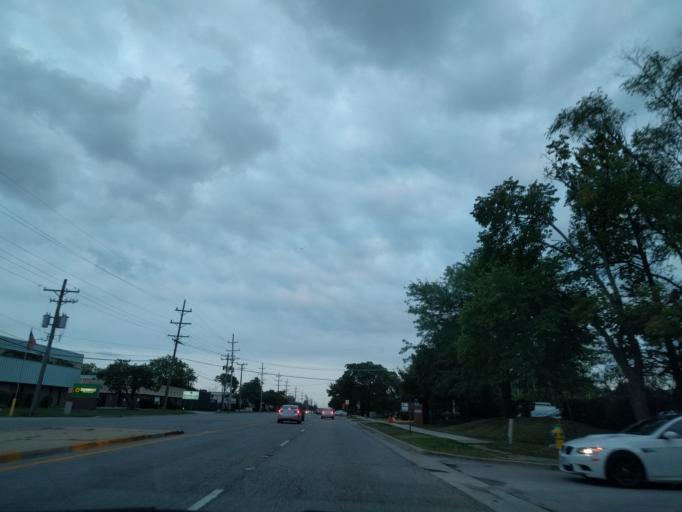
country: US
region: Illinois
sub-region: Cook County
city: Elk Grove Village
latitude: 42.0327
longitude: -87.9602
